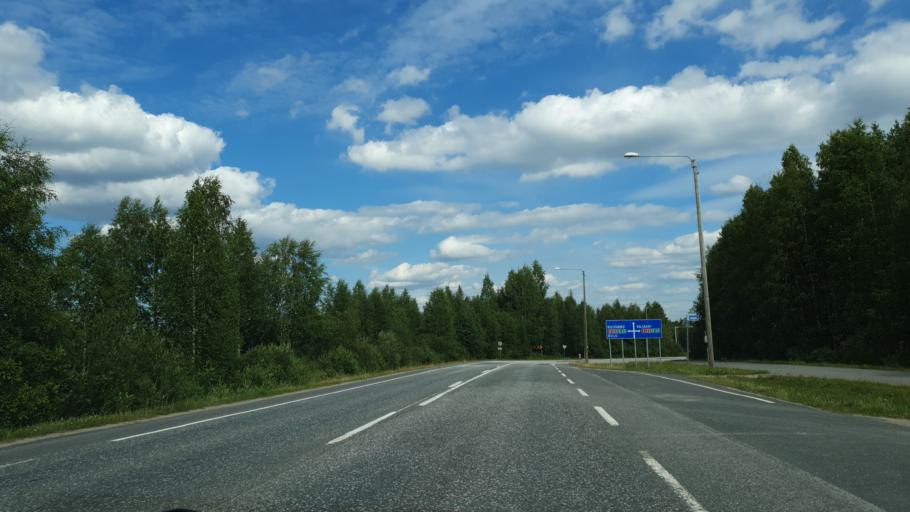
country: FI
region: Kainuu
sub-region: Kajaani
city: Kajaani
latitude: 64.2572
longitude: 27.8173
